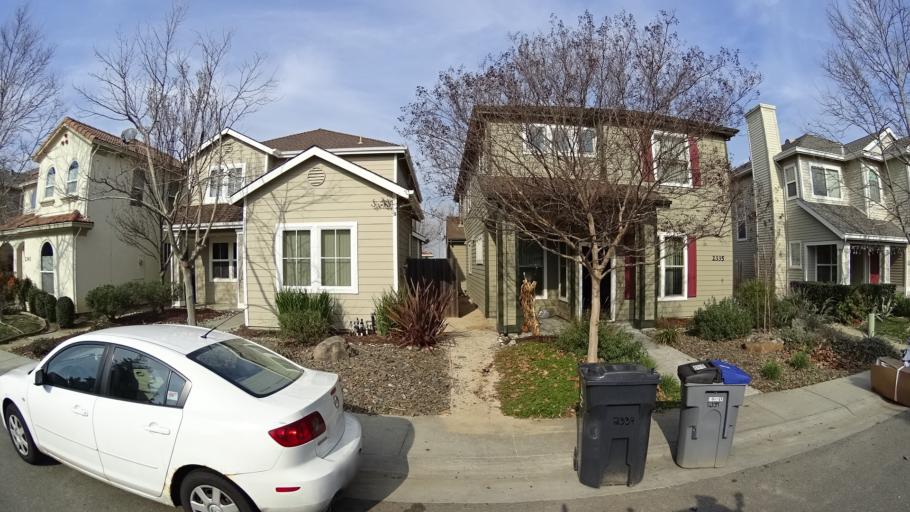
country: US
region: California
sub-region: Yolo County
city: Davis
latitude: 38.5599
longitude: -121.7806
